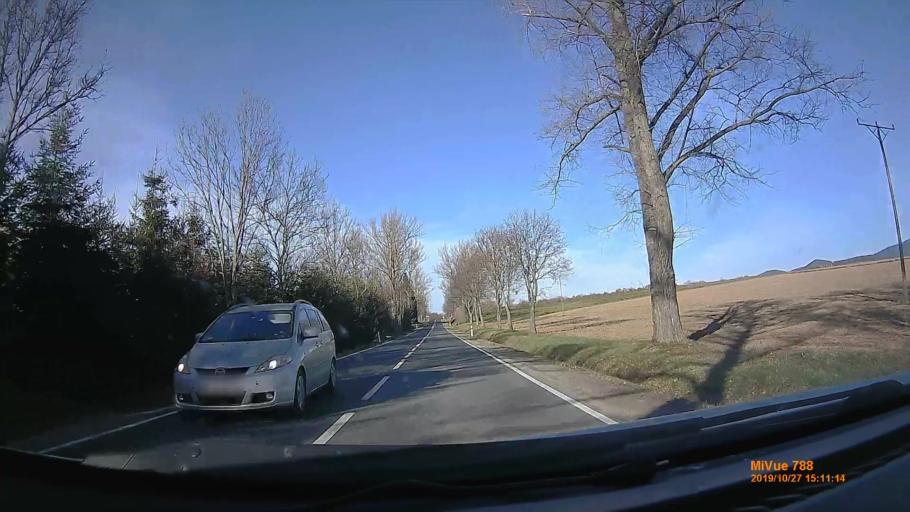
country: PL
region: Lower Silesian Voivodeship
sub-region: Powiat klodzki
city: Miedzylesie
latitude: 50.1949
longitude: 16.6711
